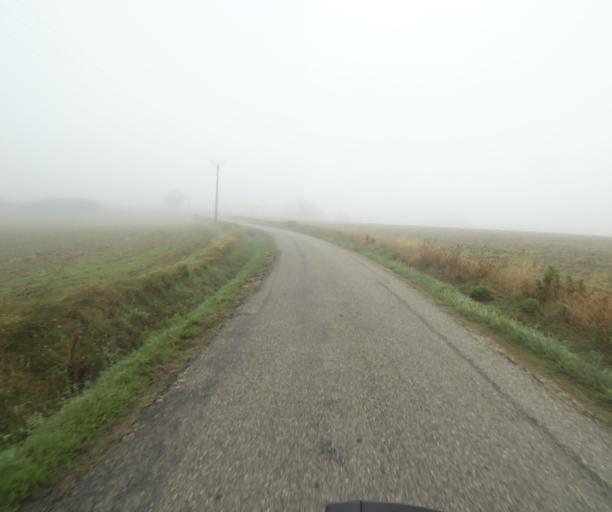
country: FR
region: Midi-Pyrenees
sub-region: Departement de la Haute-Garonne
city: Villemur-sur-Tarn
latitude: 43.9071
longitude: 1.4853
